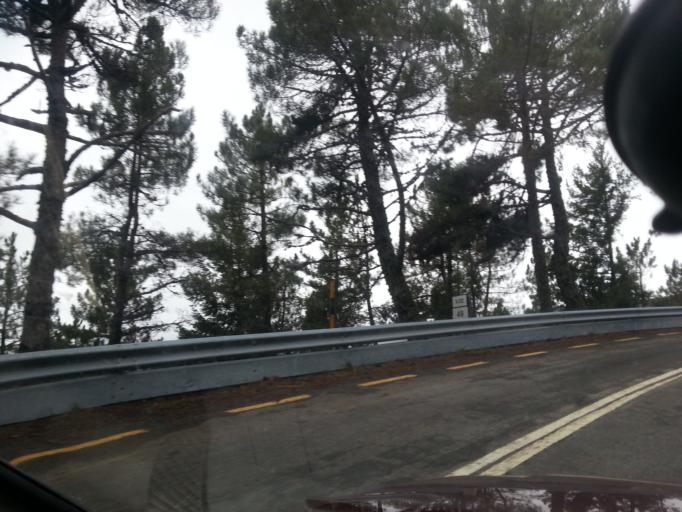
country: PT
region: Guarda
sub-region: Manteigas
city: Manteigas
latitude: 40.4172
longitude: -7.5422
